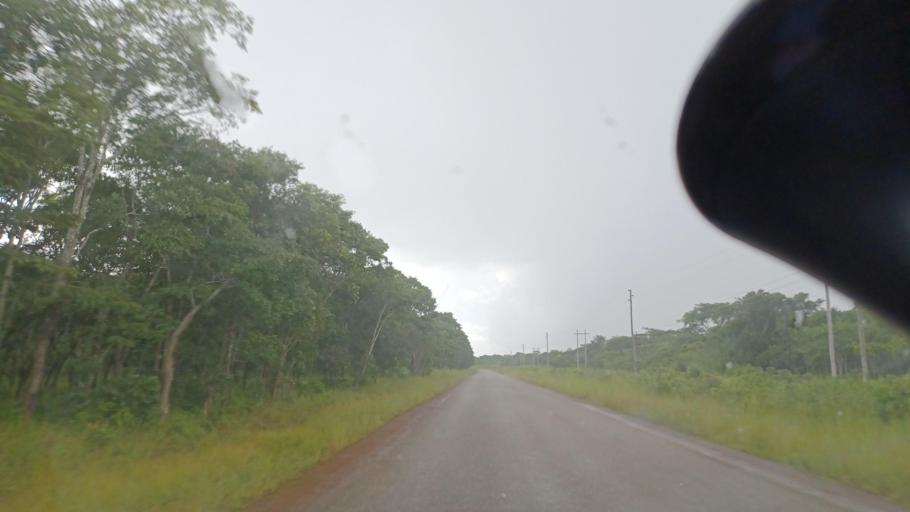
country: ZM
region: North-Western
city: Kasempa
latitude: -13.0917
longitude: 25.9300
